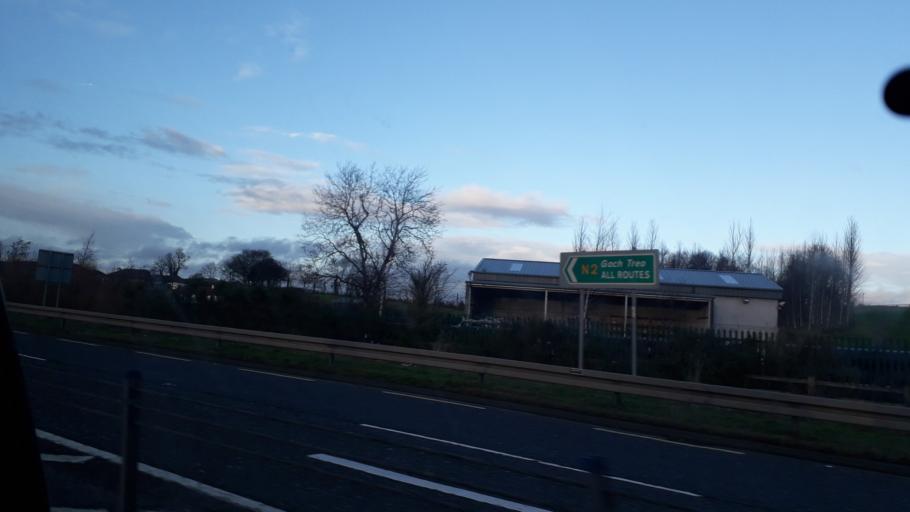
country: IE
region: Ulster
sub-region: County Monaghan
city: Castleblayney
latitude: 54.1375
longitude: -6.7775
